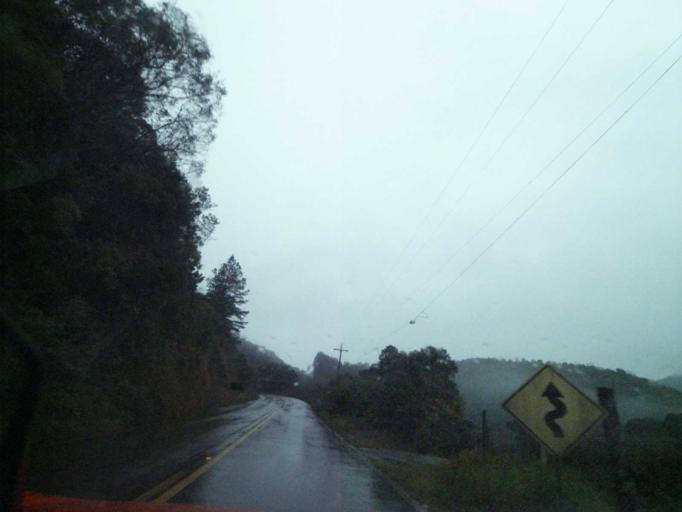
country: BR
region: Santa Catarina
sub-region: Anitapolis
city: Anitapolis
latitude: -27.8456
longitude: -49.0538
